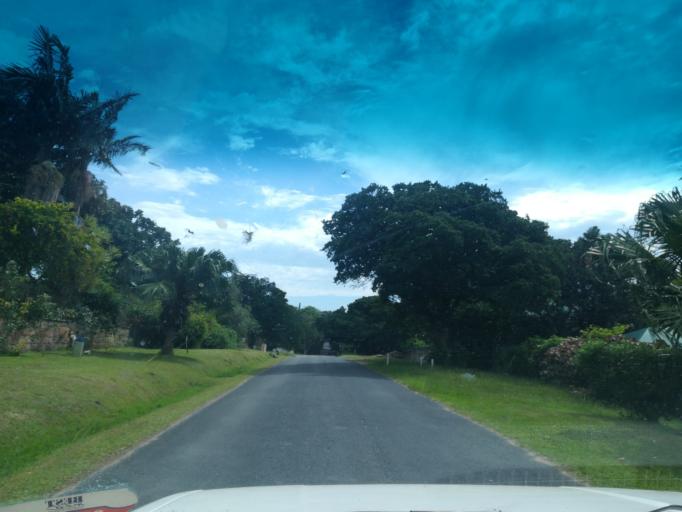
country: ZA
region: KwaZulu-Natal
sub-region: Ugu District Municipality
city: Scottburgh
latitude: -30.3879
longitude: 30.6913
